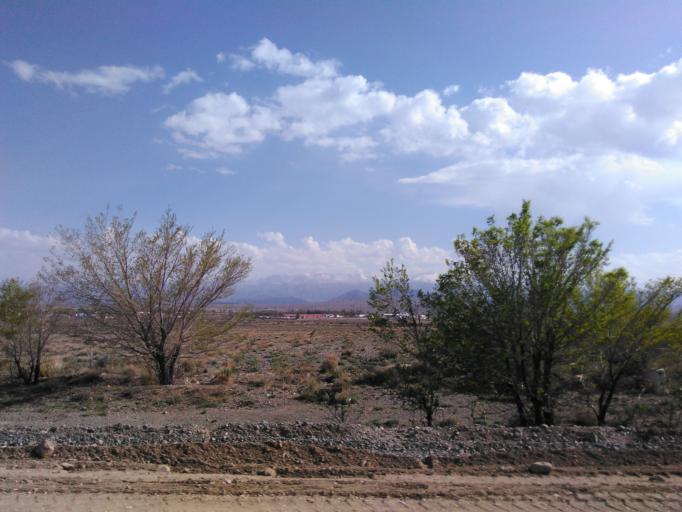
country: KG
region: Ysyk-Koel
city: Balykchy
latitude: 42.4562
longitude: 76.1443
